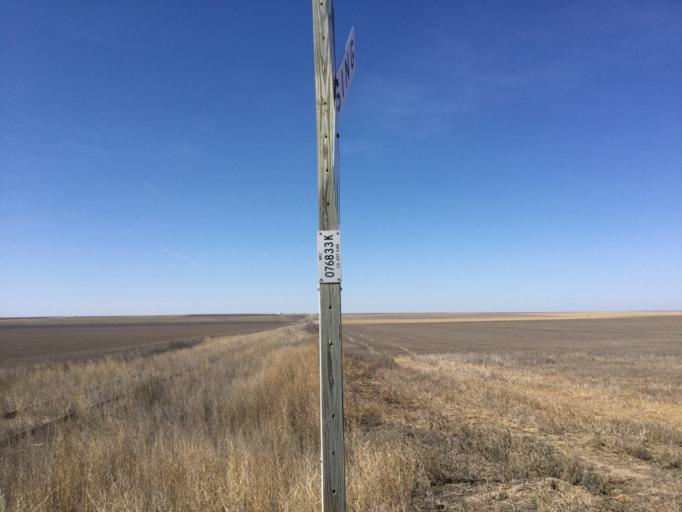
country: US
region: Kansas
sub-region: Cheyenne County
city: Saint Francis
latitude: 39.7634
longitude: -101.6363
